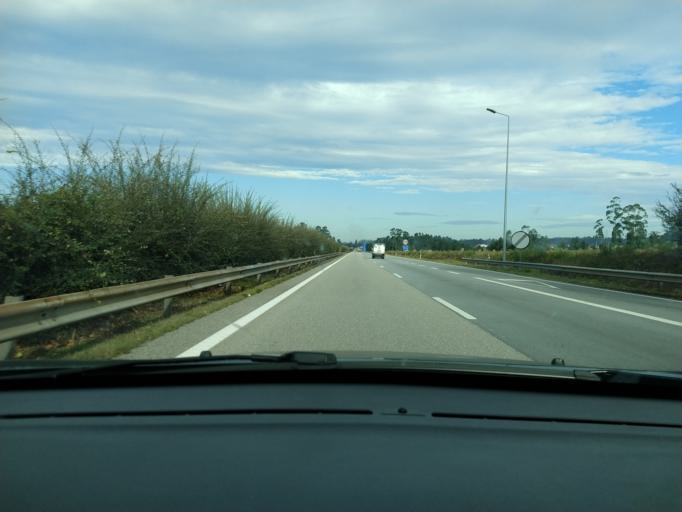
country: PT
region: Aveiro
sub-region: Estarreja
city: Beduido
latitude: 40.7559
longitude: -8.5363
